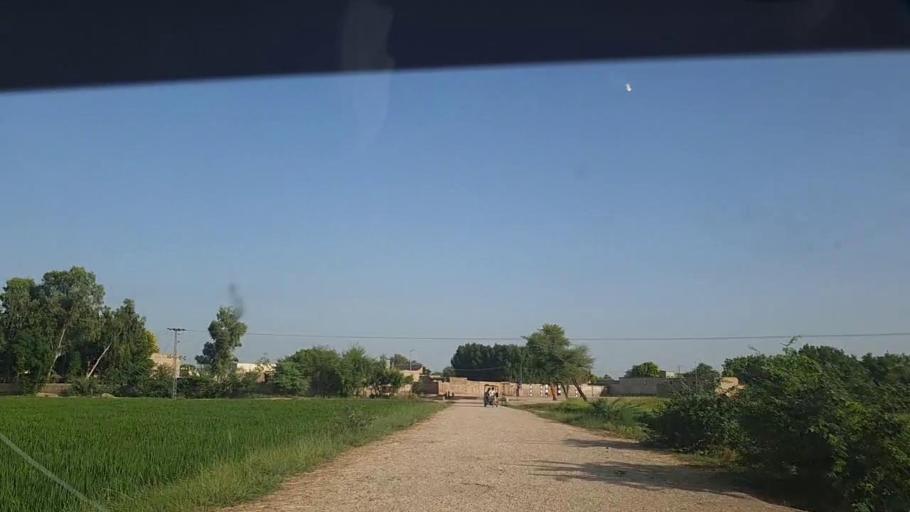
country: PK
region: Sindh
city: Tangwani
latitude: 28.2653
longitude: 69.0137
